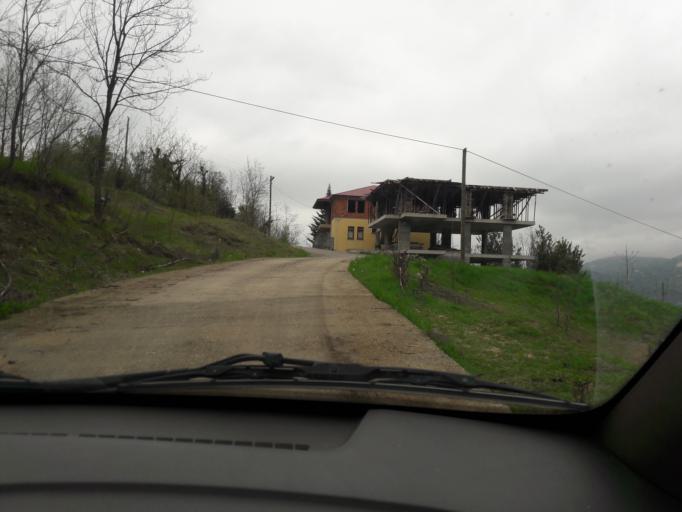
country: TR
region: Trabzon
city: Duzkoy
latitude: 40.9280
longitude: 39.4818
